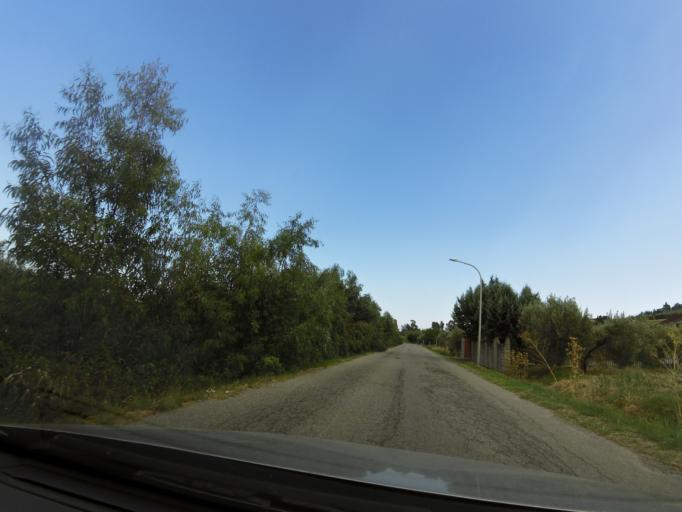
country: IT
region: Calabria
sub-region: Provincia di Reggio Calabria
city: Monasterace Marina
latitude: 38.4229
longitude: 16.5490
